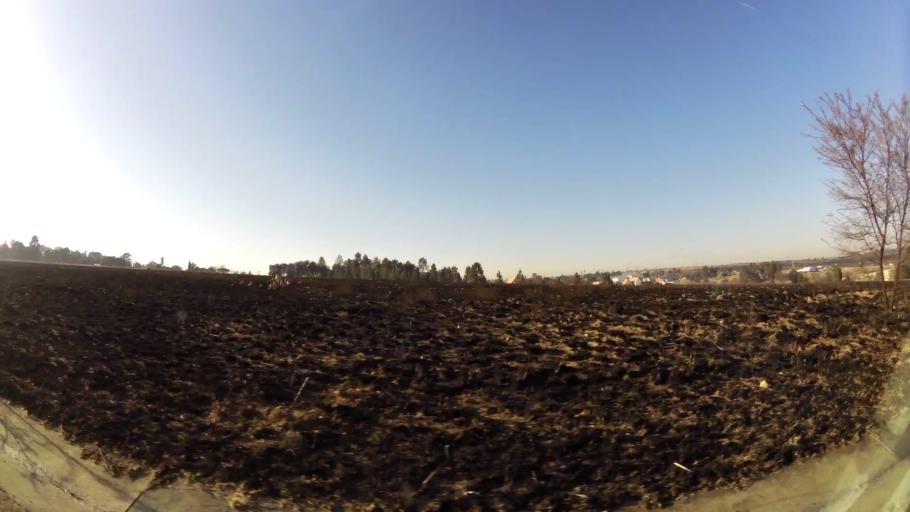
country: ZA
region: Gauteng
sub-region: City of Johannesburg Metropolitan Municipality
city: Midrand
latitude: -26.0263
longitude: 28.1372
